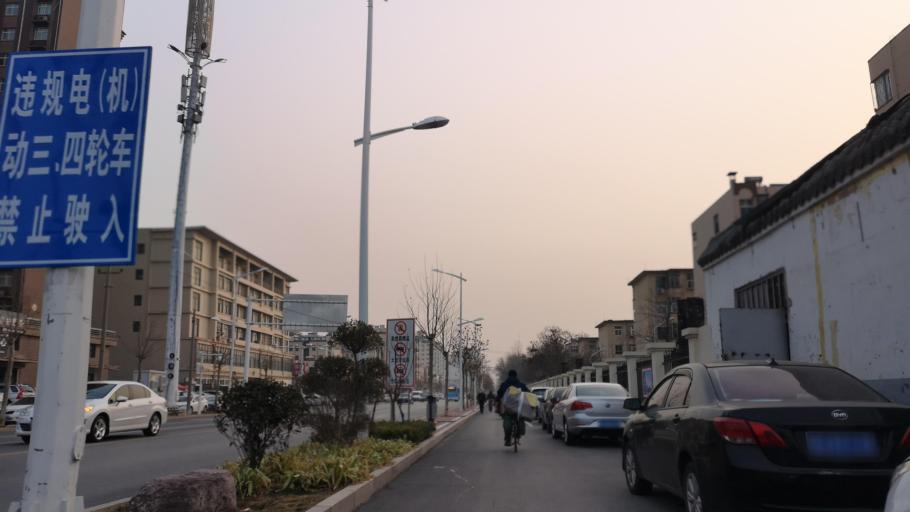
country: CN
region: Henan Sheng
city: Zhongyuanlu
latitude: 35.7892
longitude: 115.0822
